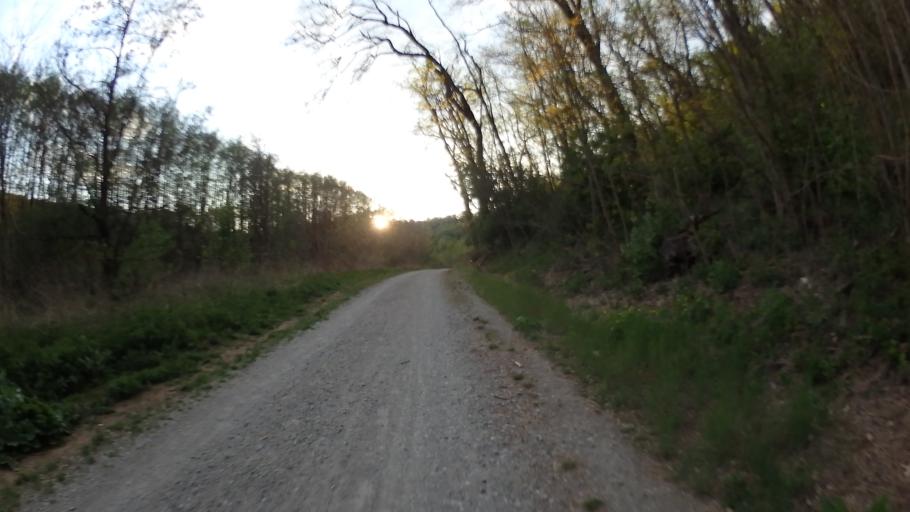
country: CZ
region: South Moravian
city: Strelice
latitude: 49.1430
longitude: 16.4830
